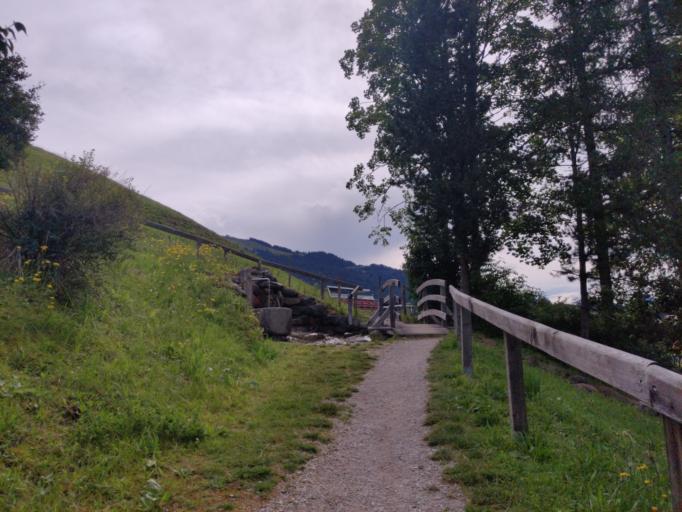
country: AT
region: Tyrol
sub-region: Politischer Bezirk Kufstein
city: Ellmau
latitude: 47.5118
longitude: 12.3043
